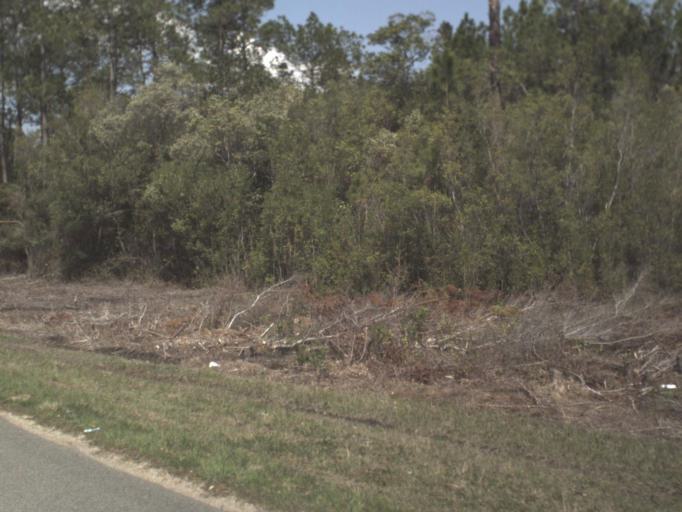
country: US
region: Florida
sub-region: Liberty County
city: Bristol
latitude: 30.4041
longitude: -84.8213
